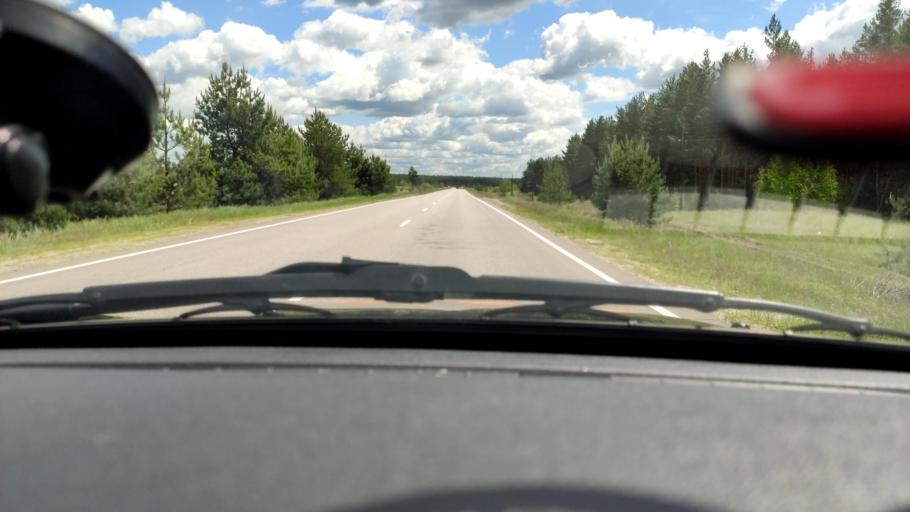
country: RU
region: Voronezj
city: Uryv-Pokrovka
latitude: 51.0529
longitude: 38.9657
